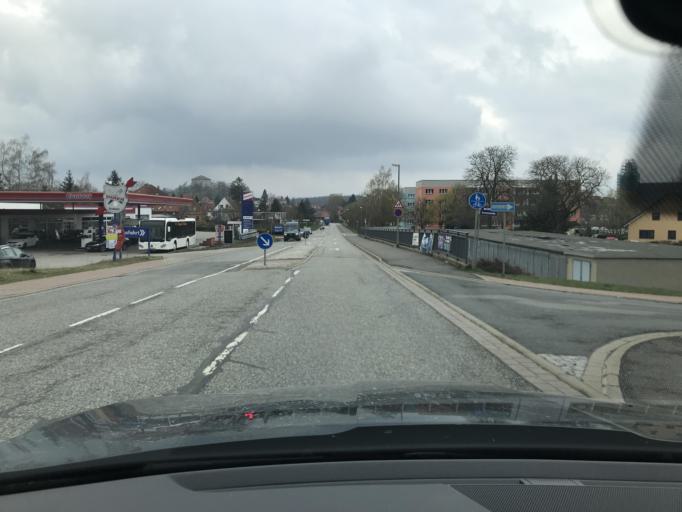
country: DE
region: Saxony-Anhalt
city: Harzgerode
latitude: 51.6378
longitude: 11.1447
